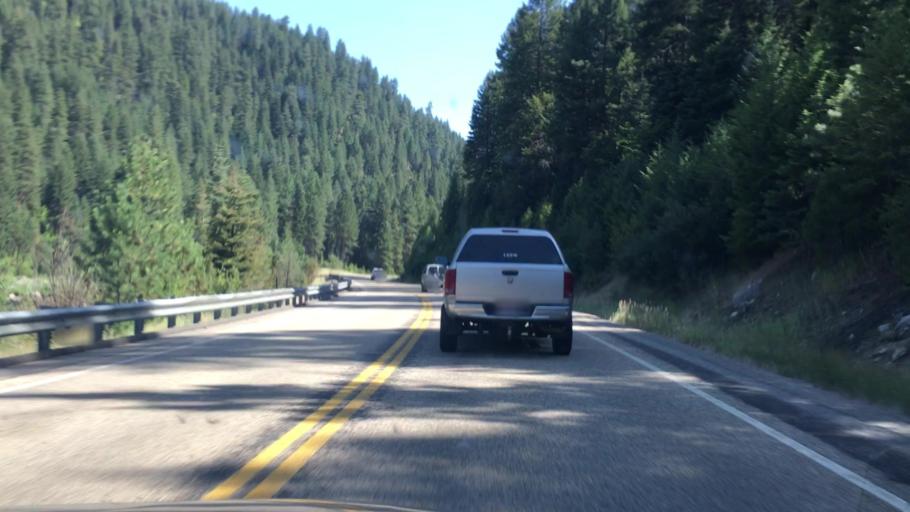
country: US
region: Idaho
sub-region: Valley County
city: Cascade
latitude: 44.1666
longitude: -116.1203
